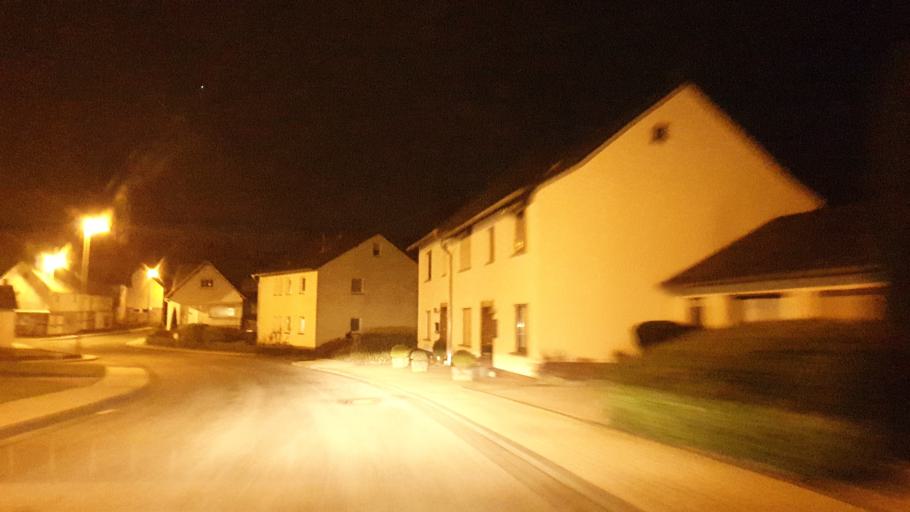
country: DE
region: Rheinland-Pfalz
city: Oberdreis
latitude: 50.6390
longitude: 7.6483
